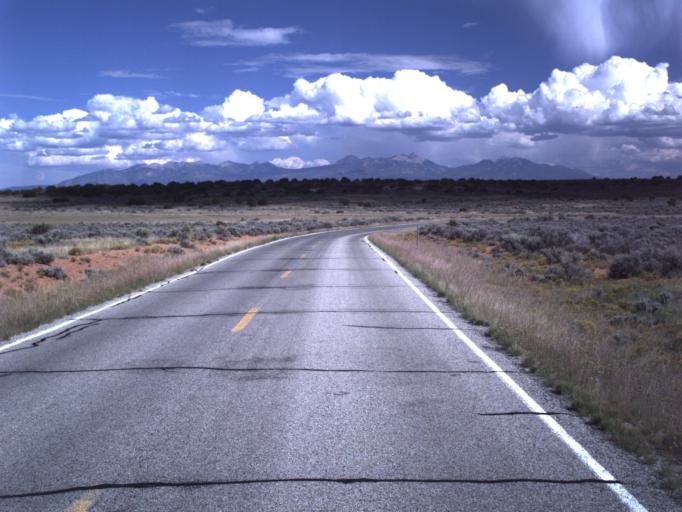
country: US
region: Utah
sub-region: Grand County
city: Moab
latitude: 38.5219
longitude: -109.7349
